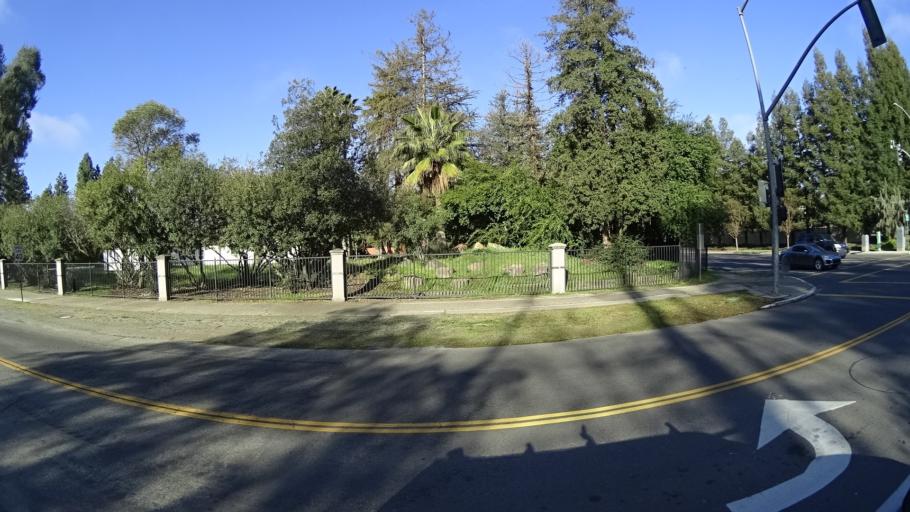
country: US
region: California
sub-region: Fresno County
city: Fresno
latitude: 36.8225
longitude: -119.8353
